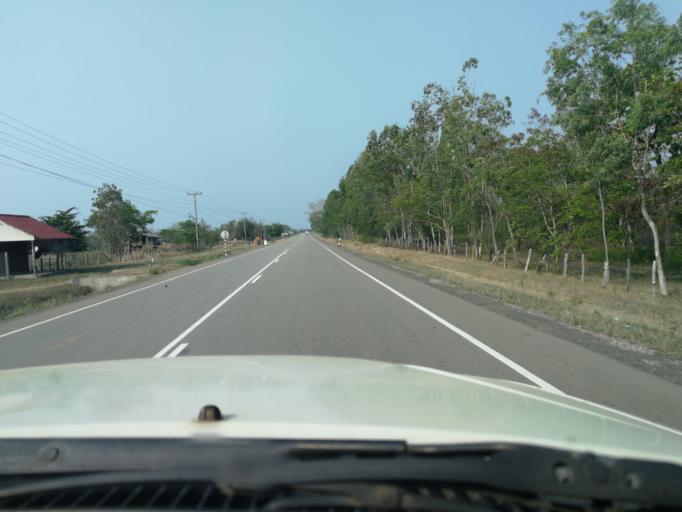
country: TH
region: Mukdahan
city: Wan Yai
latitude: 16.7116
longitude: 105.2433
